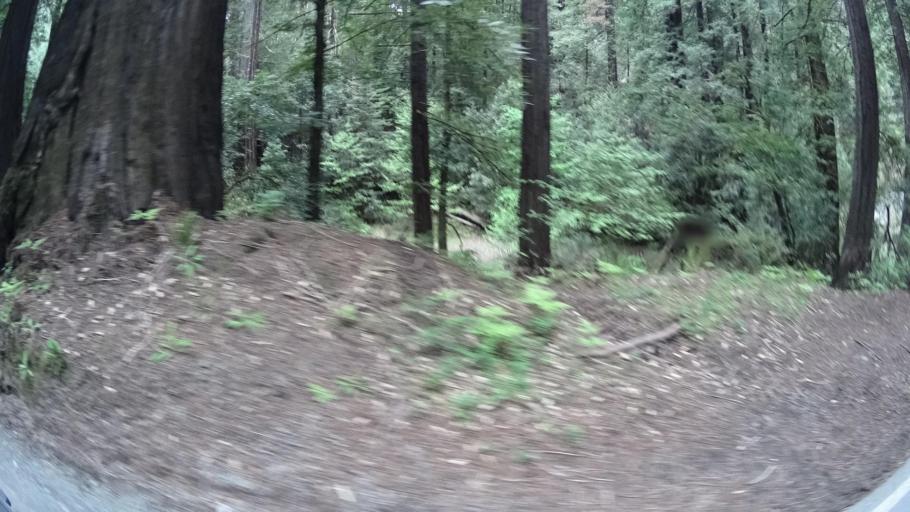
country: US
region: California
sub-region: Humboldt County
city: Redway
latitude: 40.1232
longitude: -123.8430
